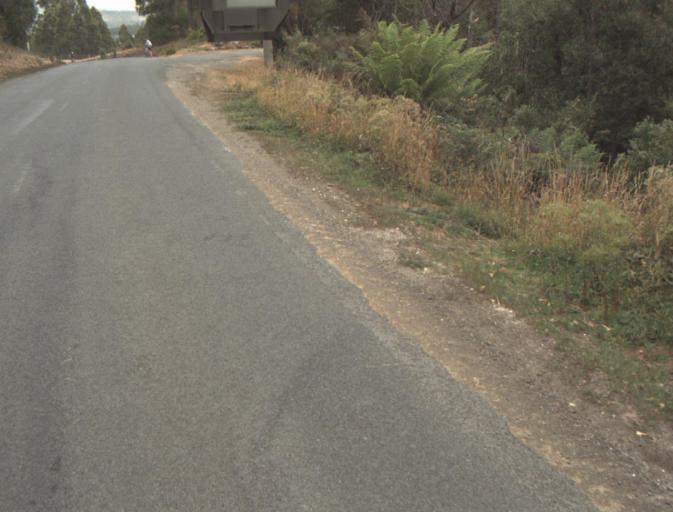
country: AU
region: Tasmania
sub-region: Launceston
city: Mayfield
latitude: -41.2149
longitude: 147.2110
